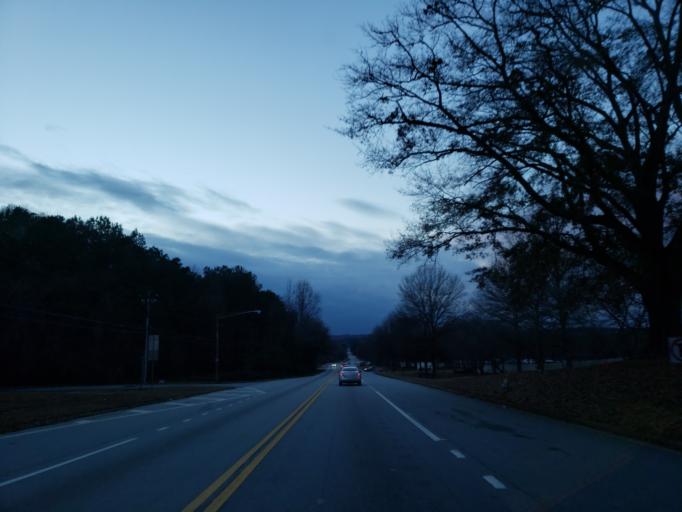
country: US
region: Georgia
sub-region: Douglas County
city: Lithia Springs
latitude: 33.6928
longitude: -84.6208
